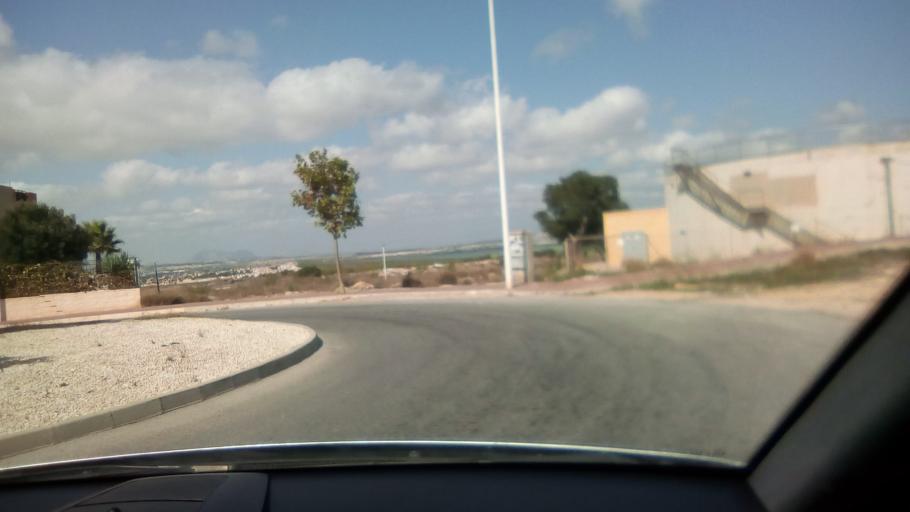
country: ES
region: Valencia
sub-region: Provincia de Alicante
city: Torrevieja
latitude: 38.0061
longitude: -0.6691
